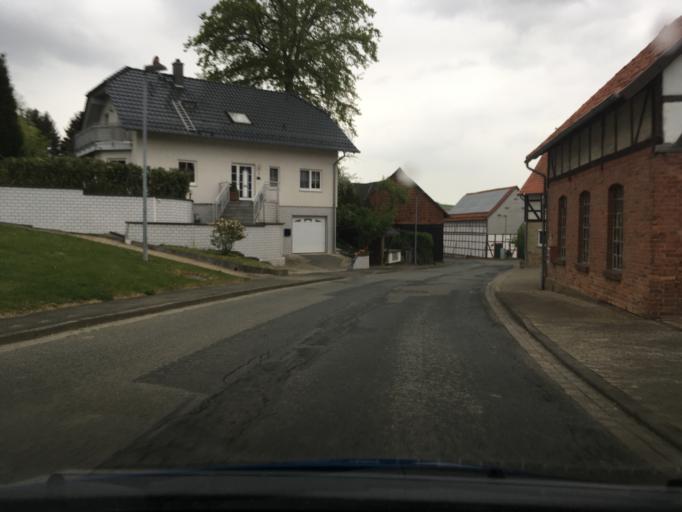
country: DE
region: Lower Saxony
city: Eimen
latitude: 51.8445
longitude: 9.8184
